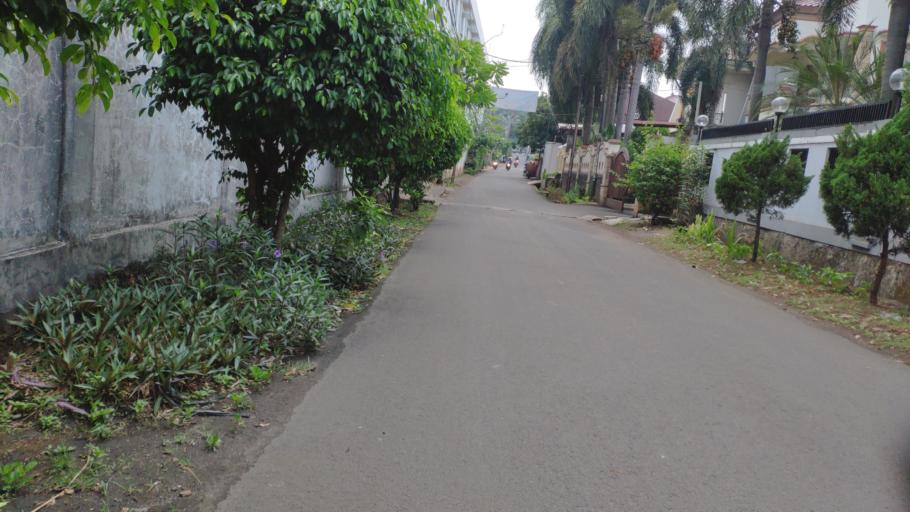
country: ID
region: West Java
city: Pamulang
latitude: -6.3040
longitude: 106.8195
